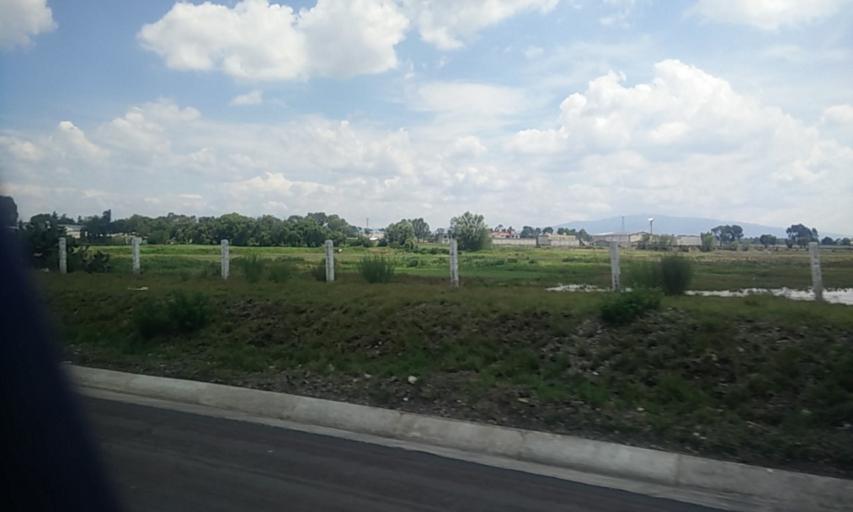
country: MX
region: Queretaro
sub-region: San Juan del Rio
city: El Cazadero
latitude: 20.2364
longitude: -99.8238
